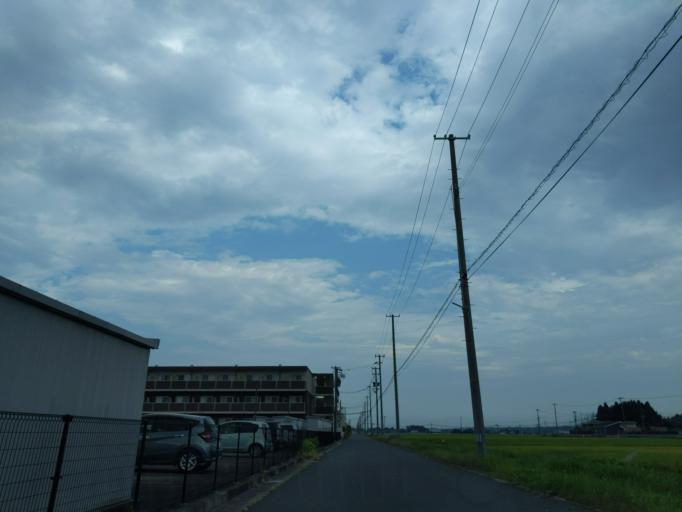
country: JP
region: Miyagi
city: Tomiya
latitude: 38.4369
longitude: 140.8747
